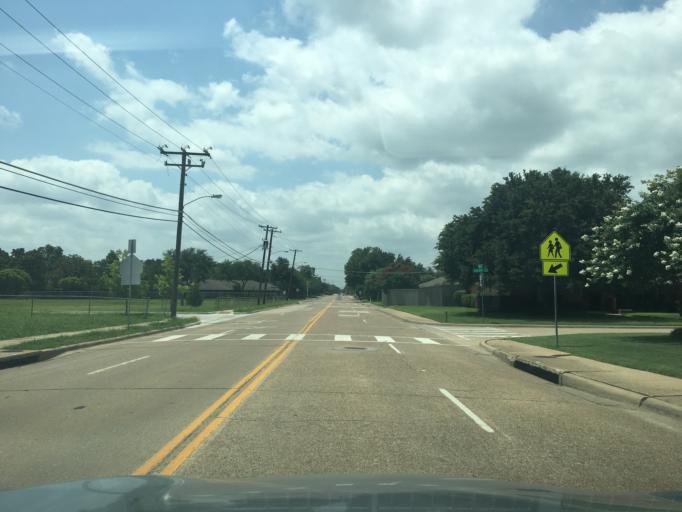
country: US
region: Texas
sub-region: Dallas County
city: Addison
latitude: 32.9218
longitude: -96.8295
